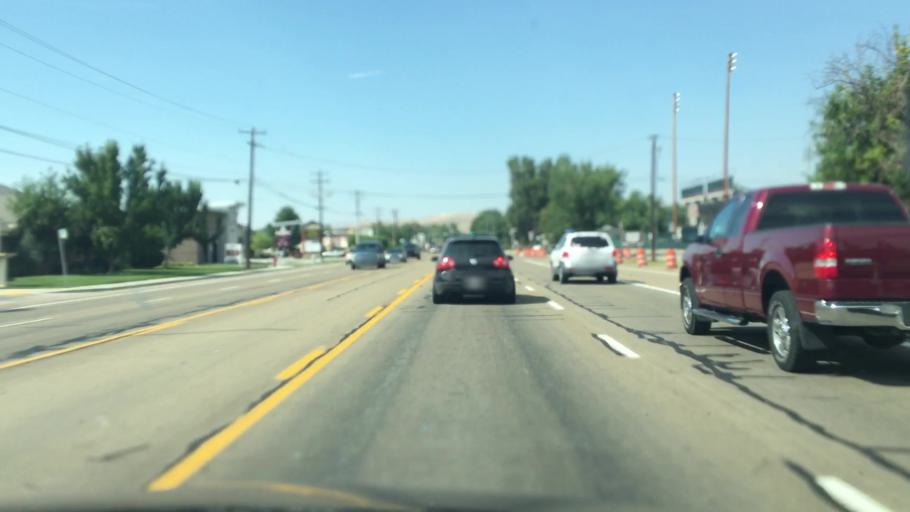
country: US
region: Idaho
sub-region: Ada County
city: Garden City
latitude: 43.6550
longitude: -116.2797
